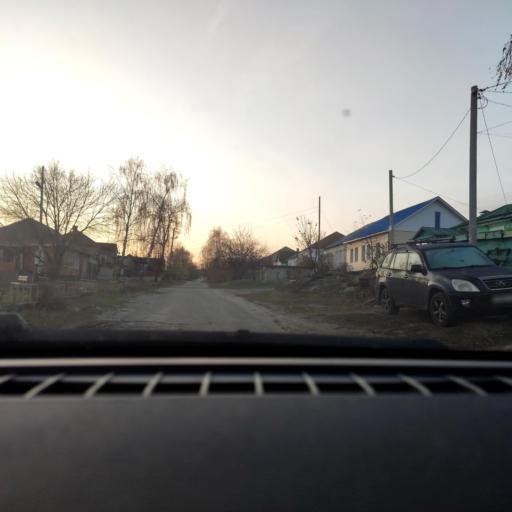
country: RU
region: Voronezj
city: Voronezh
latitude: 51.7050
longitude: 39.2651
